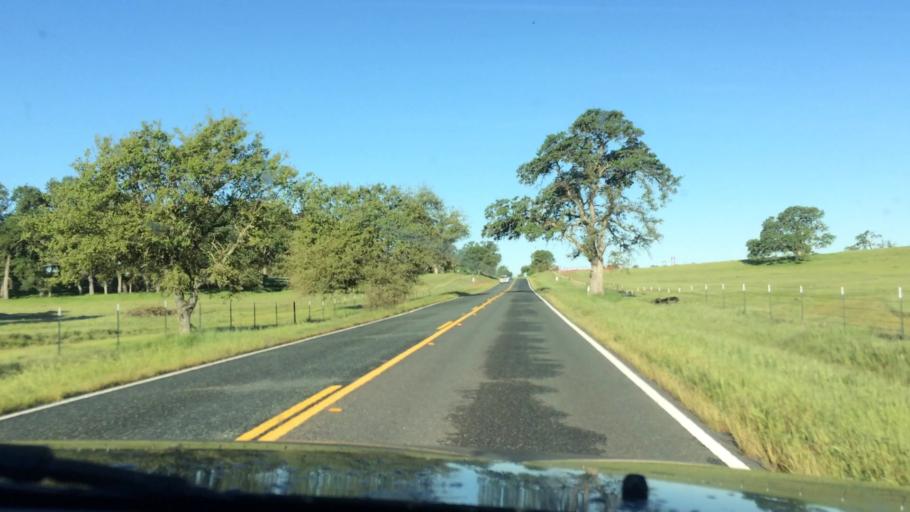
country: US
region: California
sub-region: Amador County
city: Ione
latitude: 38.3862
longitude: -121.0392
